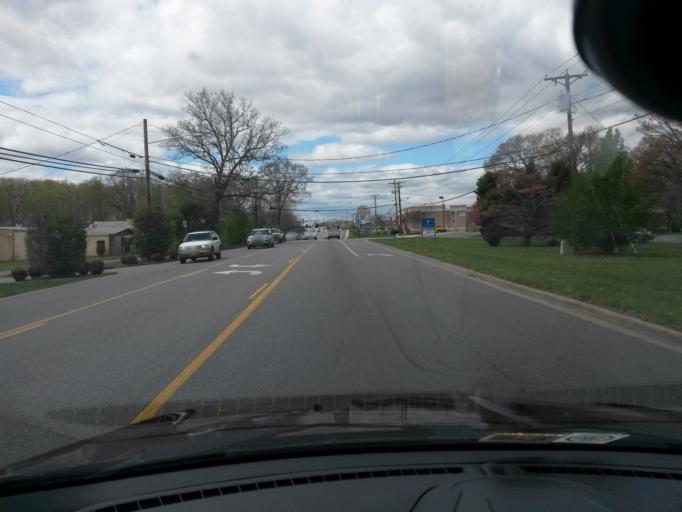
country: US
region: Virginia
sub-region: City of Lynchburg
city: West Lynchburg
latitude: 37.3980
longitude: -79.2192
